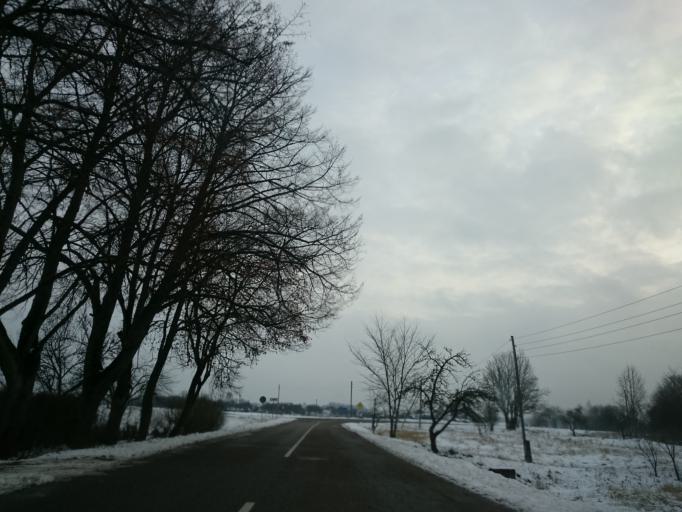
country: LV
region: Seja
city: Loja
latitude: 57.1997
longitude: 24.5959
